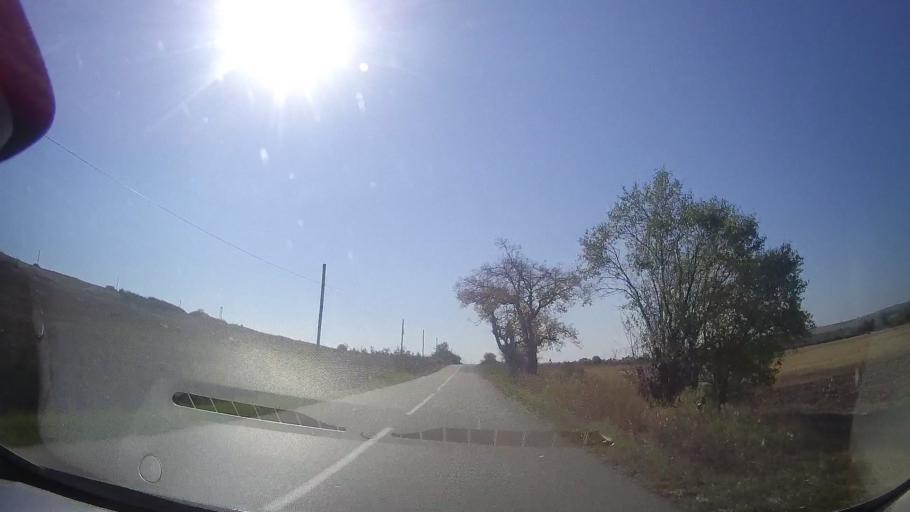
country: RO
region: Timis
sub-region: Comuna Bethausen
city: Bethausen
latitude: 45.8497
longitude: 21.9637
